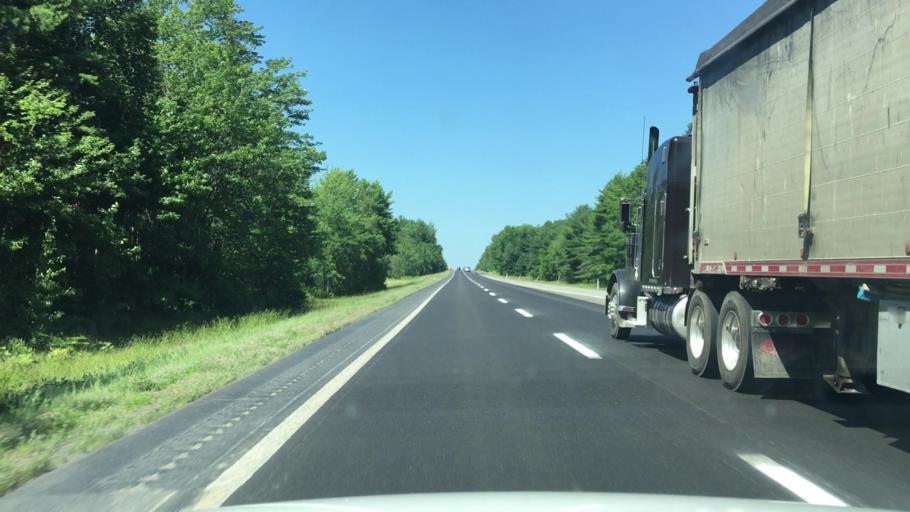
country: US
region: Maine
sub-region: Penobscot County
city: Milford
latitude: 44.9622
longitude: -68.7065
